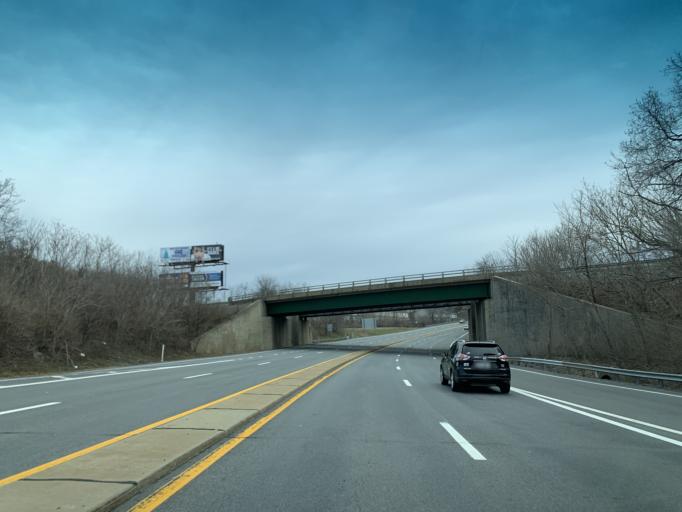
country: US
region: West Virginia
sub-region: Berkeley County
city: Martinsburg
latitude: 39.4422
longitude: -77.9703
